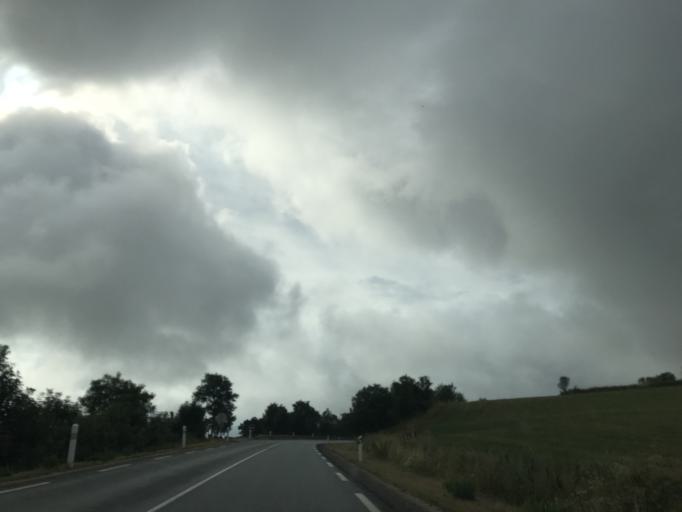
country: FR
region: Auvergne
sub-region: Departement de la Haute-Loire
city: Polignac
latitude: 45.0764
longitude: 3.8425
